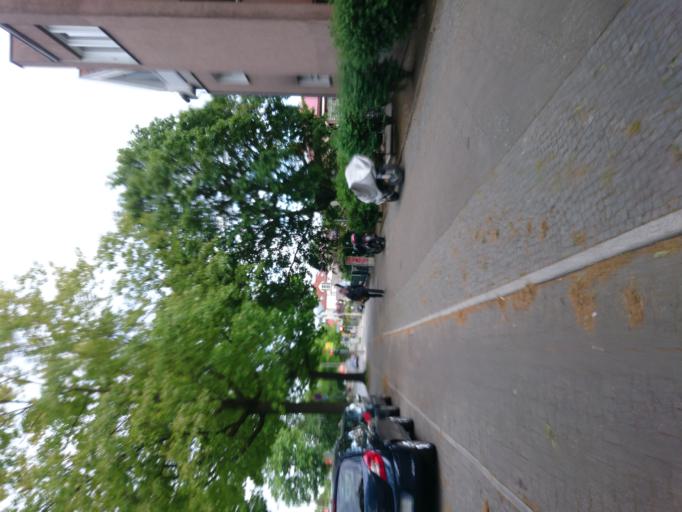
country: DE
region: Berlin
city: Waidmannslust
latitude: 52.6024
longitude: 13.3290
